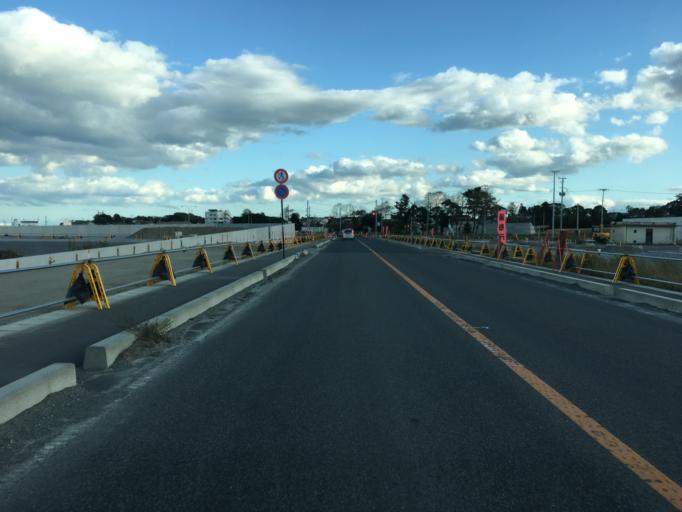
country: JP
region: Miyagi
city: Marumori
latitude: 37.8324
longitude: 140.9573
